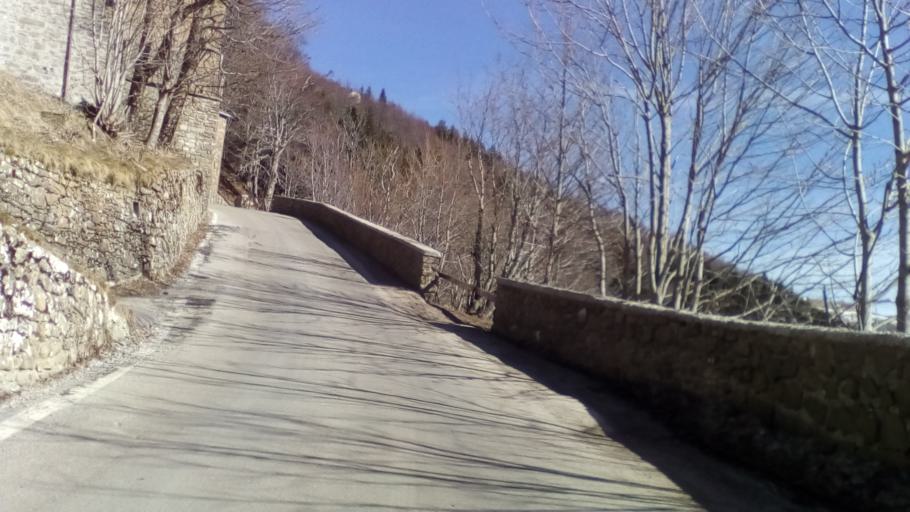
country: IT
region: Tuscany
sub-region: Provincia di Lucca
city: Fosciandora
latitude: 44.1894
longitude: 10.4806
